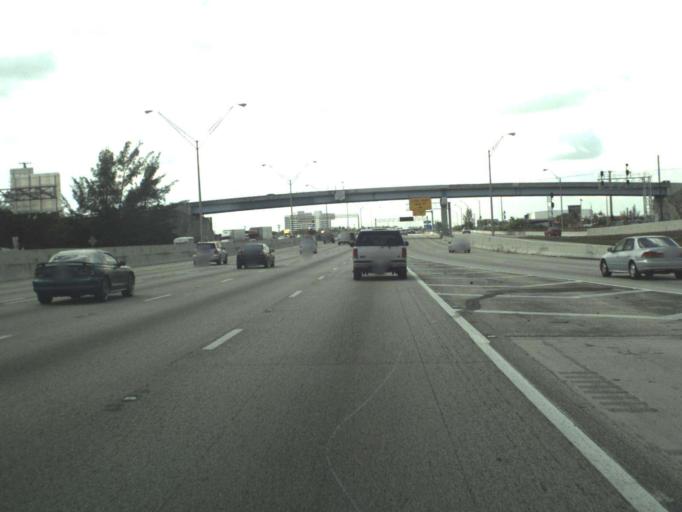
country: US
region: Florida
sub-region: Broward County
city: Dania Beach
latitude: 26.0722
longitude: -80.1671
